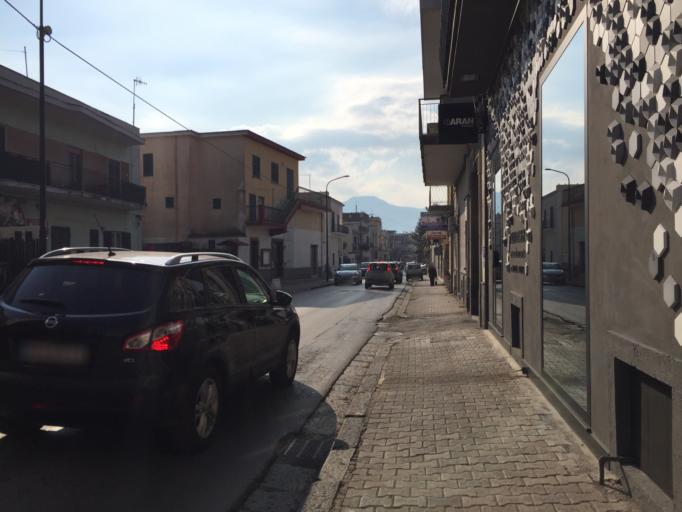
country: IT
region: Campania
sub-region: Provincia di Napoli
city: Pompei
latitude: 40.7541
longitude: 14.4987
